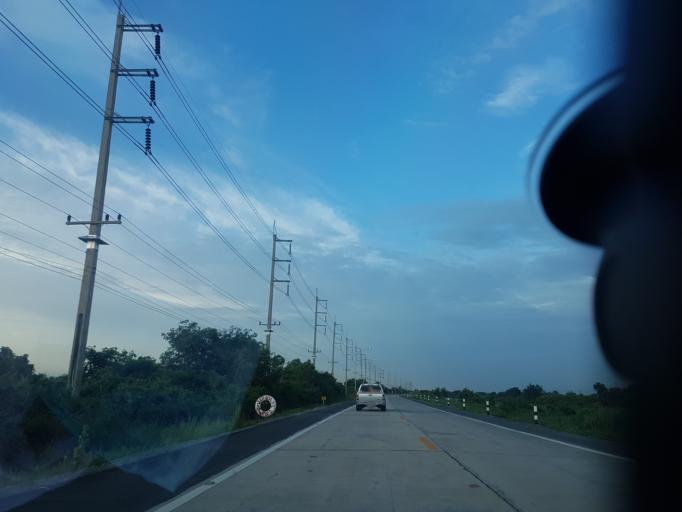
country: TH
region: Phra Nakhon Si Ayutthaya
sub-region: Amphoe Tha Ruea
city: Tha Ruea
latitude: 14.5360
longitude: 100.7499
